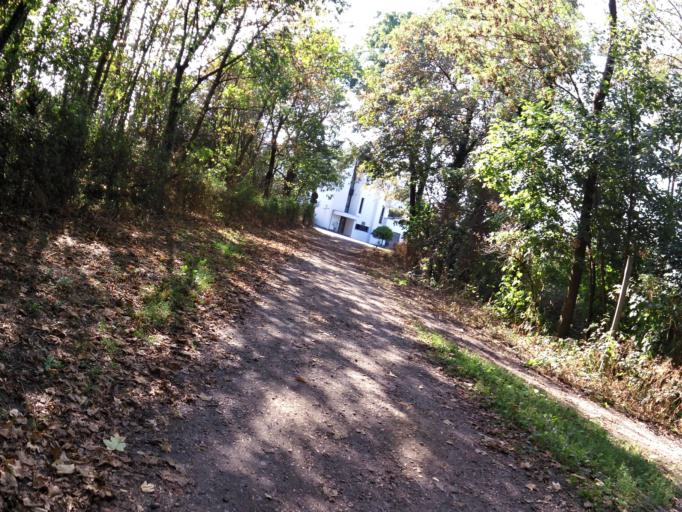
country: DE
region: North Rhine-Westphalia
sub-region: Regierungsbezirk Koln
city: Herzogenrath
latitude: 50.8498
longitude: 6.0945
